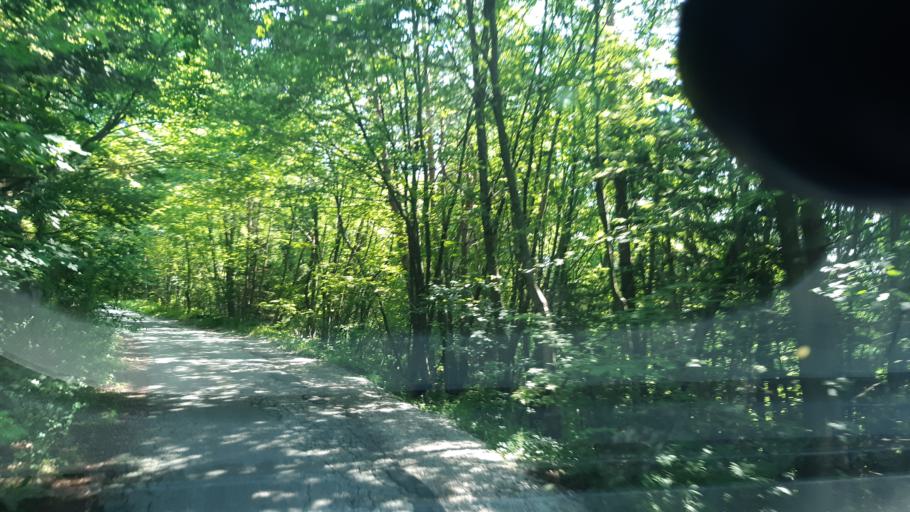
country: SI
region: Trzic
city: Bistrica pri Trzicu
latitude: 46.3606
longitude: 14.2770
